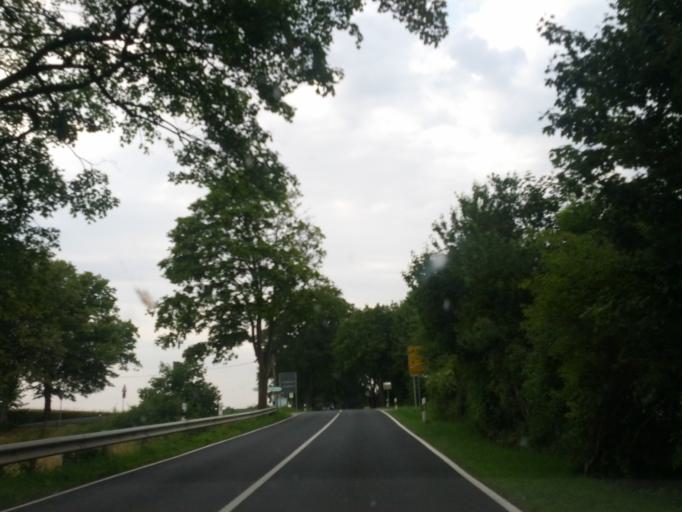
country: DE
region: Mecklenburg-Vorpommern
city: Kropelin
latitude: 54.0193
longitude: 11.8015
